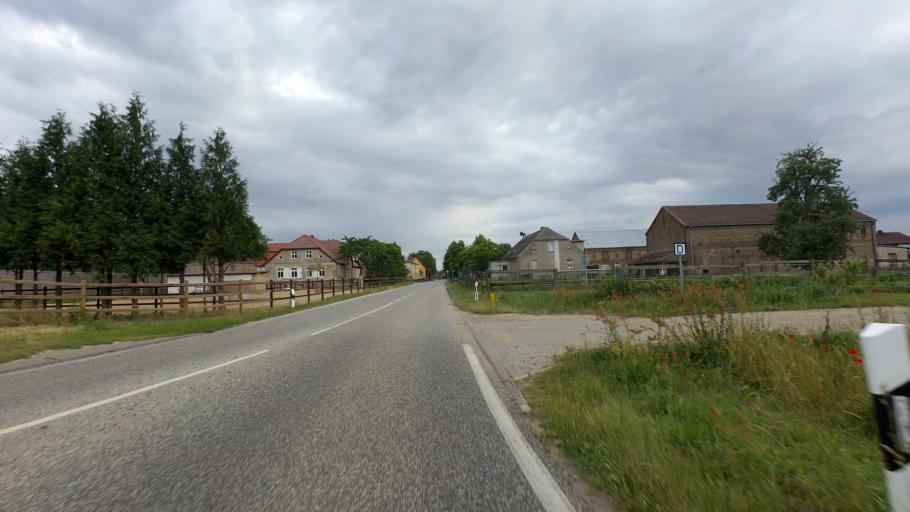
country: DE
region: Brandenburg
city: Pawesin
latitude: 52.5468
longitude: 12.7648
